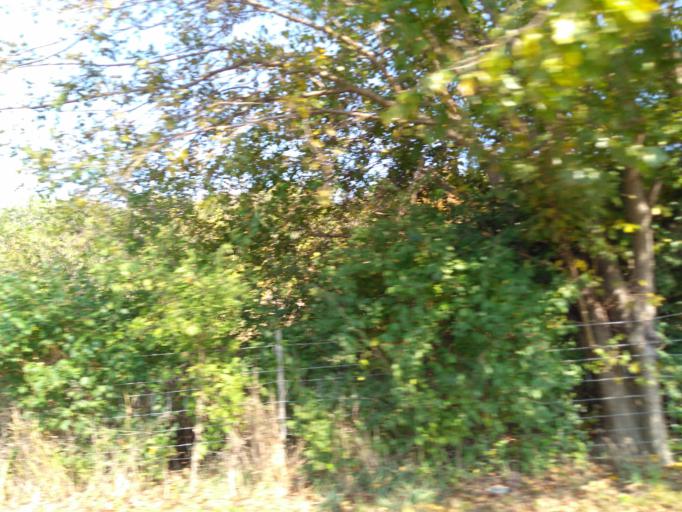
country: US
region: Missouri
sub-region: Jefferson County
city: High Ridge
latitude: 38.5069
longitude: -90.5625
